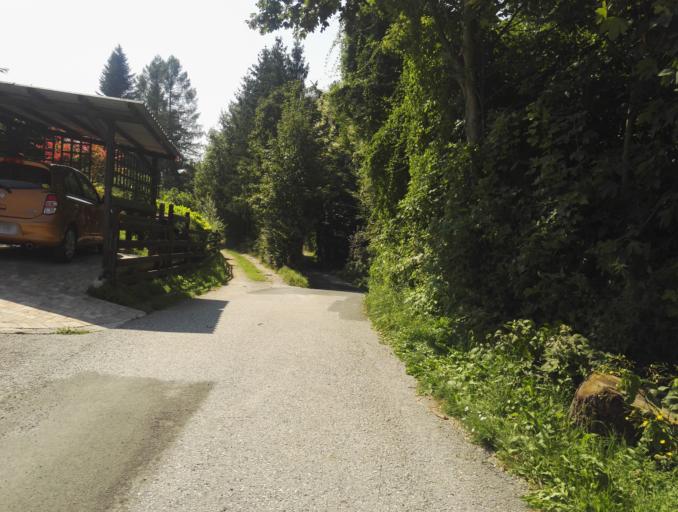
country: AT
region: Styria
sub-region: Politischer Bezirk Graz-Umgebung
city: Sankt Oswald bei Plankenwarth
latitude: 47.0951
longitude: 15.2859
